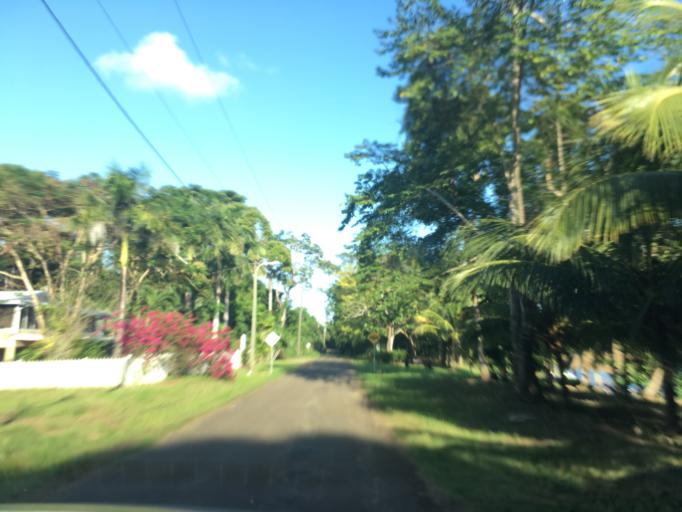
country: BZ
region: Stann Creek
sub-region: Dangriga
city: Dangriga
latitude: 16.8227
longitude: -88.3180
